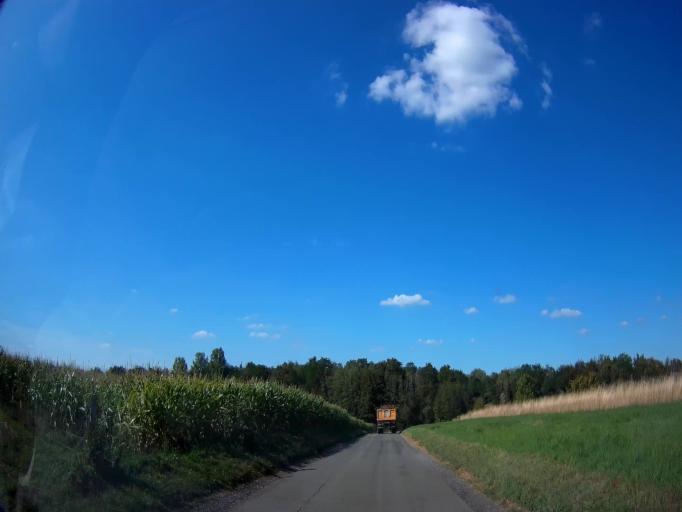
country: BE
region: Wallonia
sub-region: Province de Namur
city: Dinant
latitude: 50.2379
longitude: 4.9673
